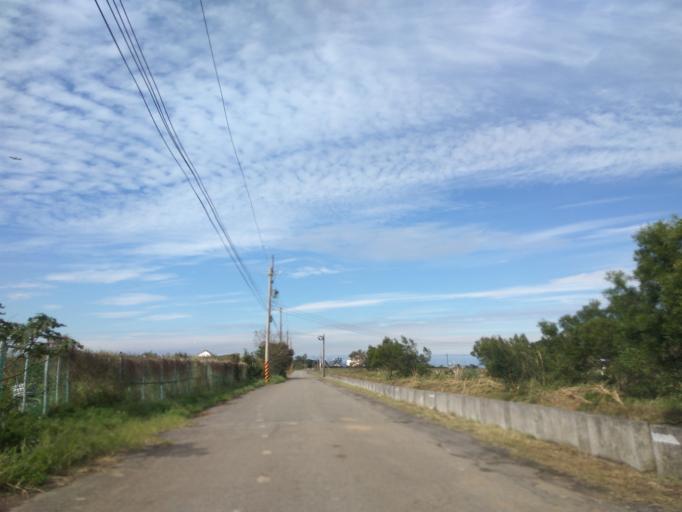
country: TW
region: Taiwan
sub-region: Hsinchu
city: Zhubei
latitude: 25.0061
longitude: 121.0786
